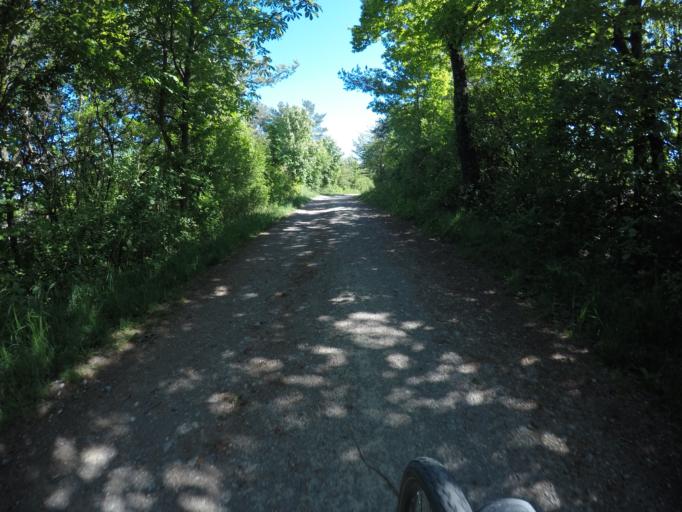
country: DE
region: Baden-Wuerttemberg
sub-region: Regierungsbezirk Stuttgart
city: Weissach
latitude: 48.8327
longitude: 8.8997
